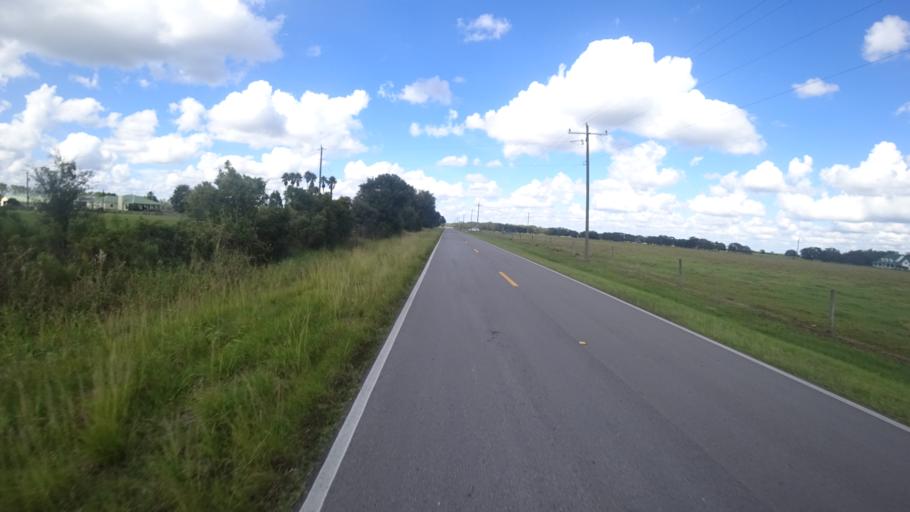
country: US
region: Florida
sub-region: Sarasota County
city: Warm Mineral Springs
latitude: 27.2784
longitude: -82.2110
